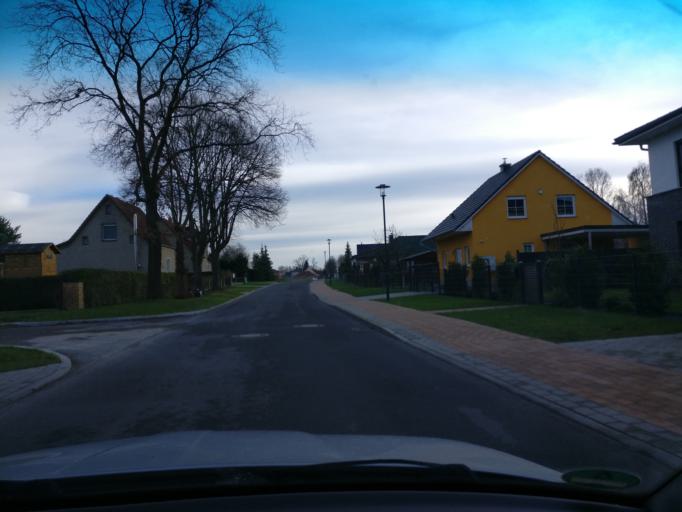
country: DE
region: Brandenburg
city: Bernau bei Berlin
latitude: 52.6805
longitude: 13.5355
